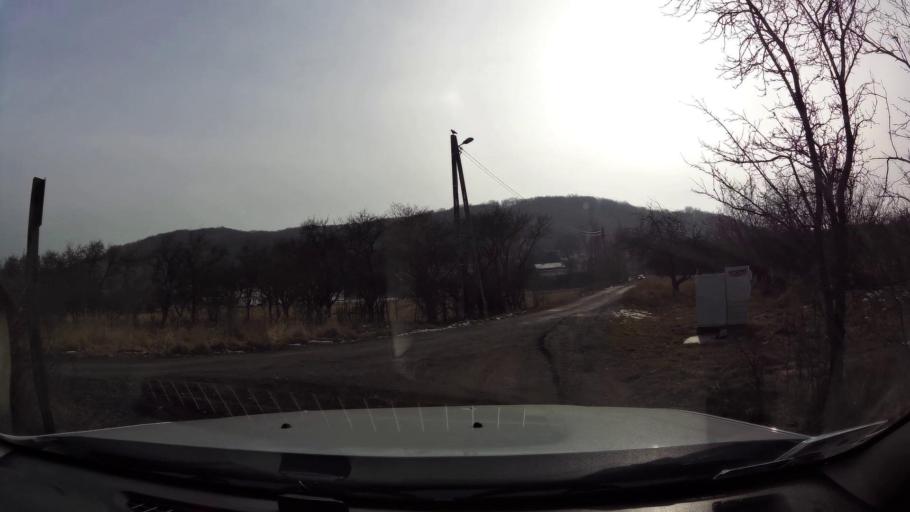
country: PL
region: West Pomeranian Voivodeship
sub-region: Powiat kamienski
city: Miedzyzdroje
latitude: 53.8803
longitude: 14.4480
